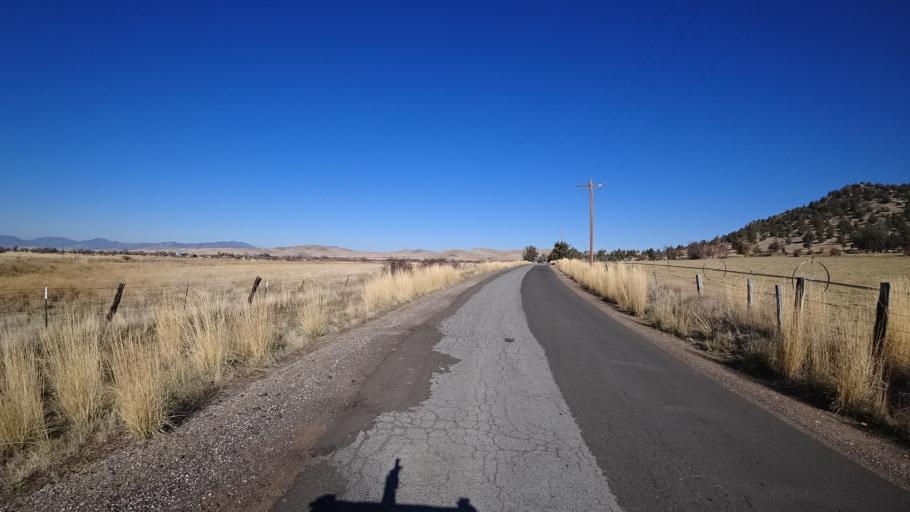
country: US
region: California
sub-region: Siskiyou County
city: Montague
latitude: 41.7055
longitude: -122.3793
